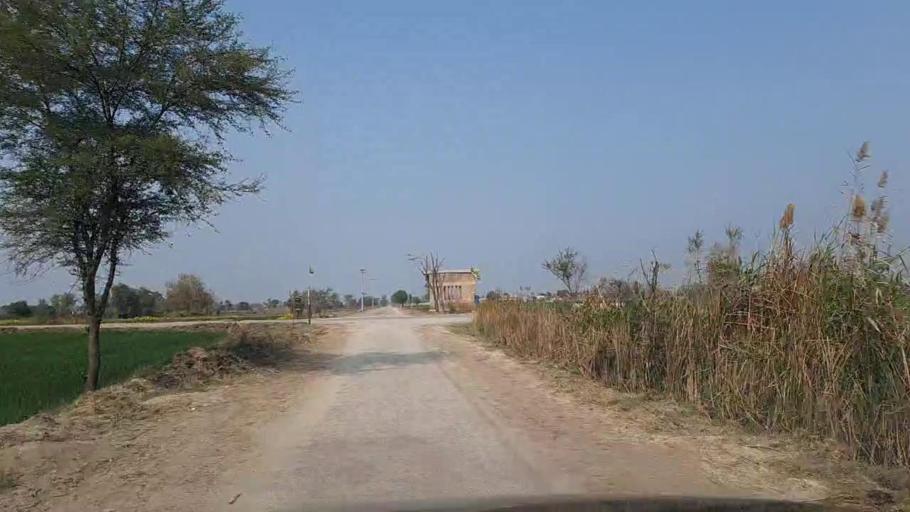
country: PK
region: Sindh
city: Daur
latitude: 26.4040
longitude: 68.4240
